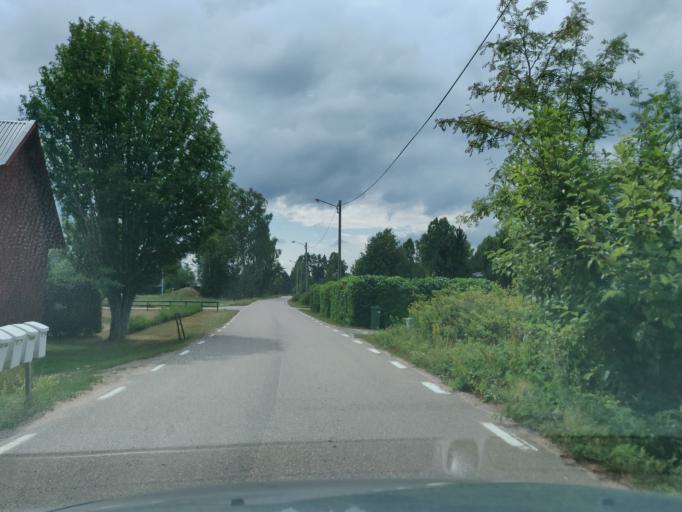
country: SE
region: Vaermland
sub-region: Munkfors Kommun
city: Munkfors
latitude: 59.8832
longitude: 13.5605
